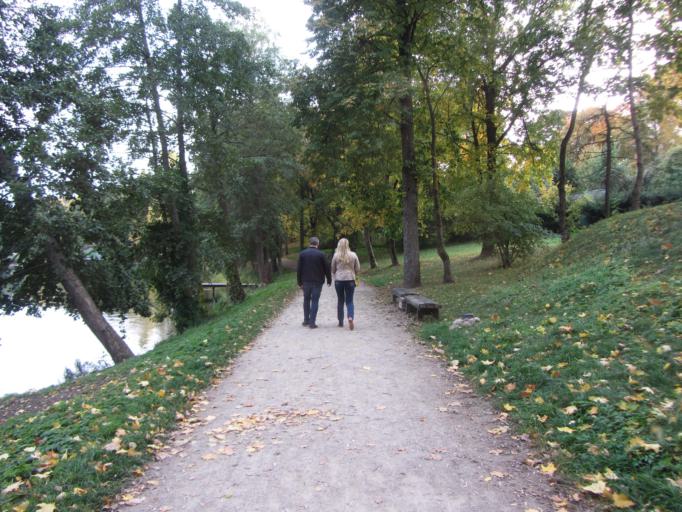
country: LT
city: Trakai
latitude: 54.6438
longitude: 24.9358
